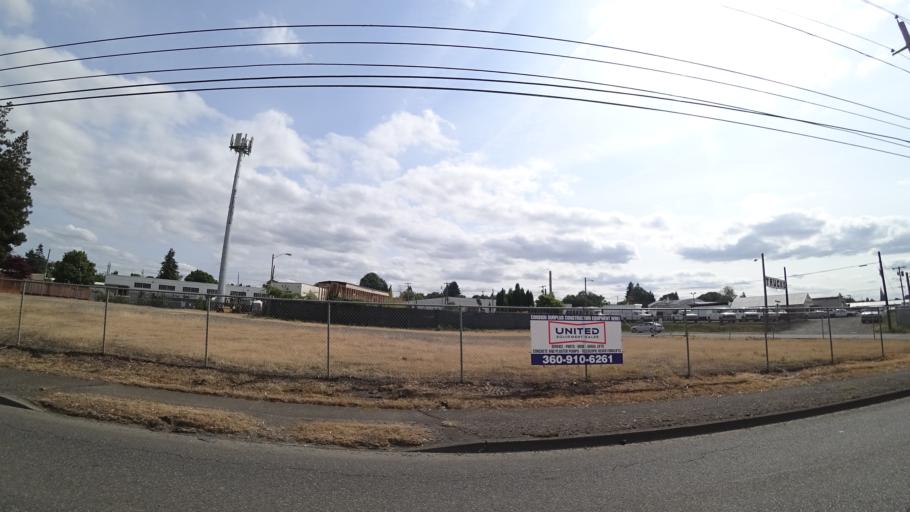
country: US
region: Oregon
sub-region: Multnomah County
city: Portland
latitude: 45.5786
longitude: -122.6530
